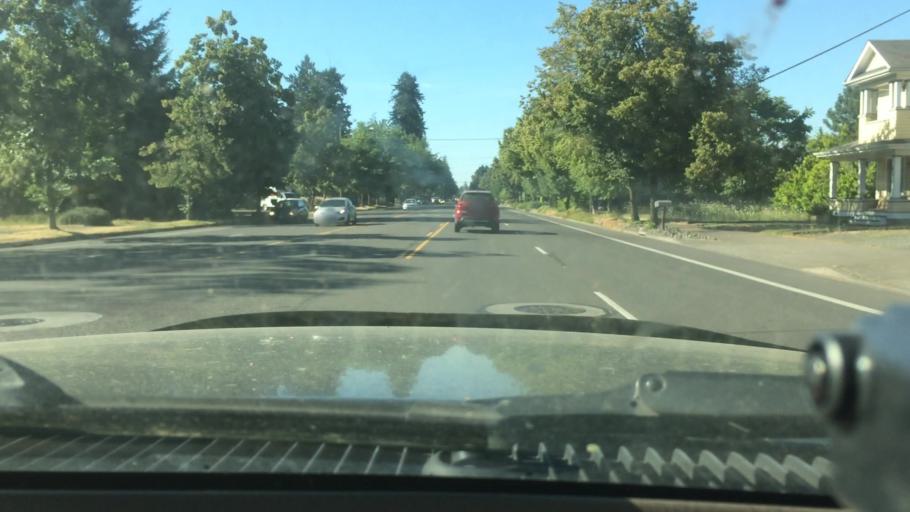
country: US
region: Oregon
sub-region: Lane County
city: Eugene
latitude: 44.0668
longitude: -123.1176
